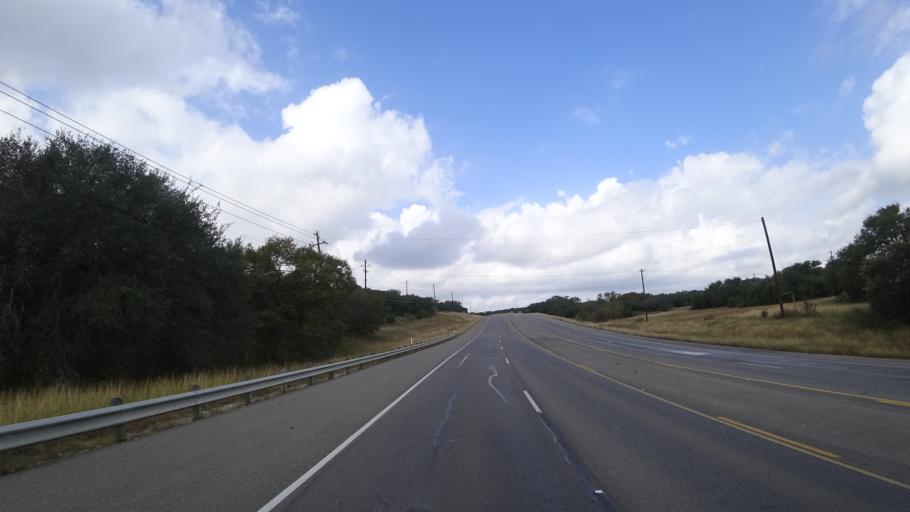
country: US
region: Texas
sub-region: Travis County
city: Barton Creek
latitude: 30.3066
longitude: -97.9026
